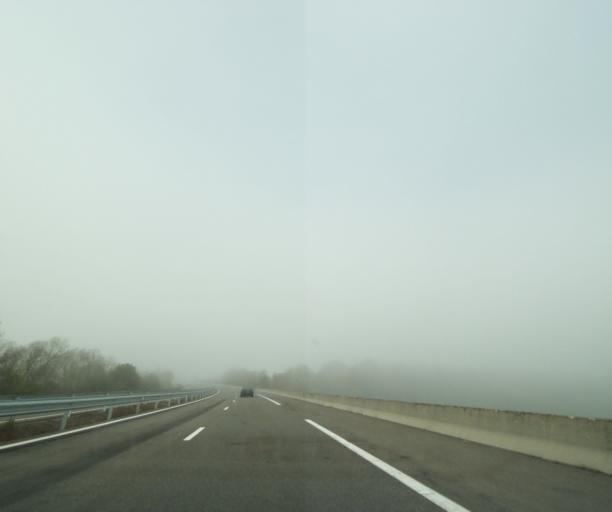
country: FR
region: Lorraine
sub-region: Departement de la Meuse
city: Dugny-sur-Meuse
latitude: 49.1161
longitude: 5.4010
